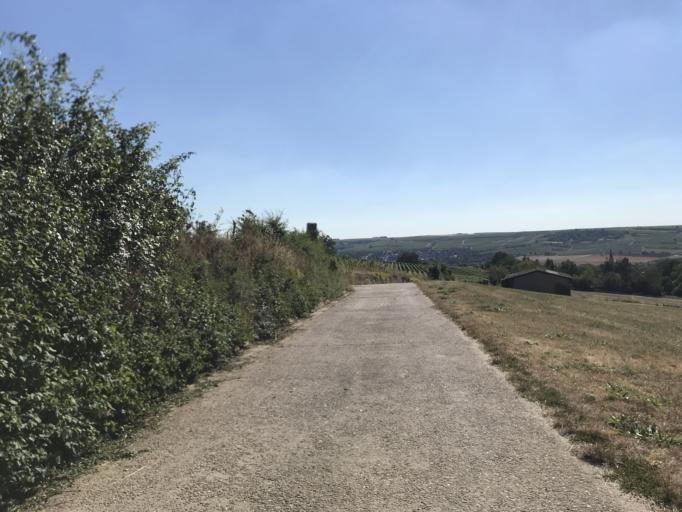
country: DE
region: Rheinland-Pfalz
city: Schwabenheim
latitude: 49.9340
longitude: 8.1071
